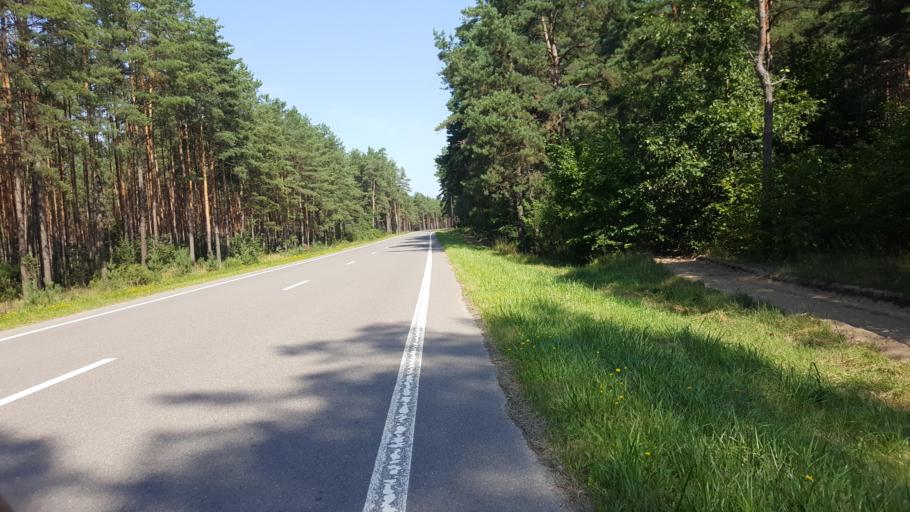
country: BY
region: Brest
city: Kamyanyuki
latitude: 52.5120
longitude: 23.6591
